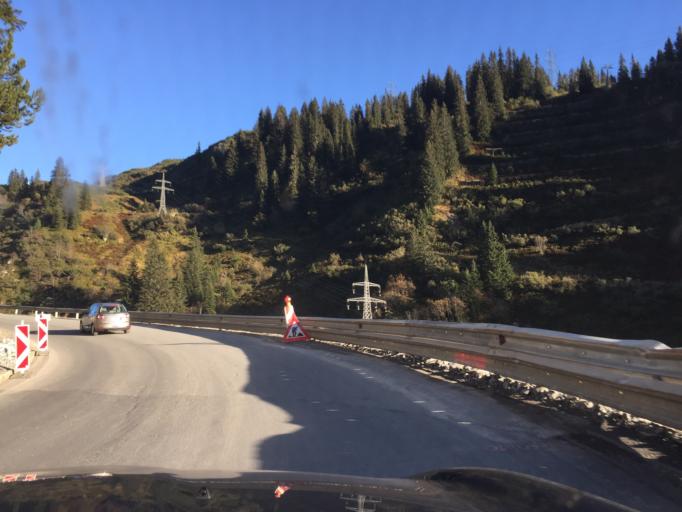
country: AT
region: Vorarlberg
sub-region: Politischer Bezirk Bludenz
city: Lech
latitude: 47.1379
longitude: 10.1635
